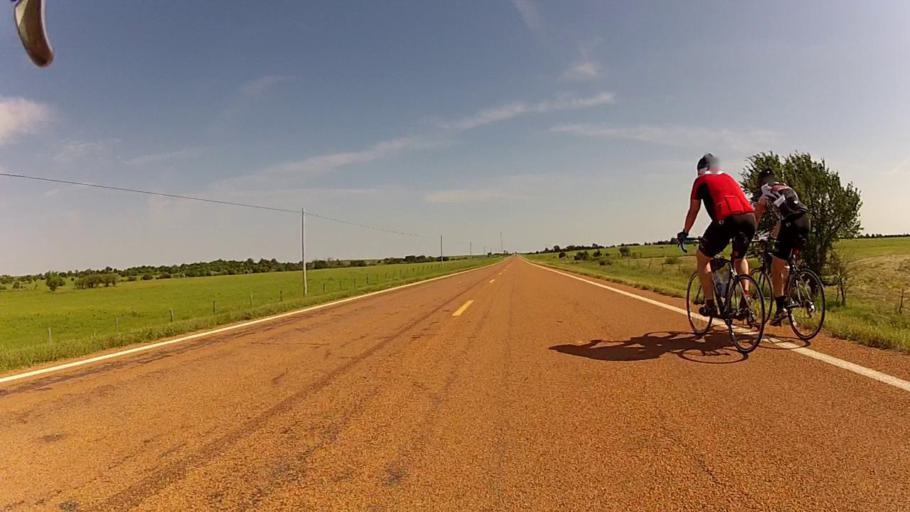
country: US
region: Kansas
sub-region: Cowley County
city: Winfield
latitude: 37.0957
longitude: -96.6436
